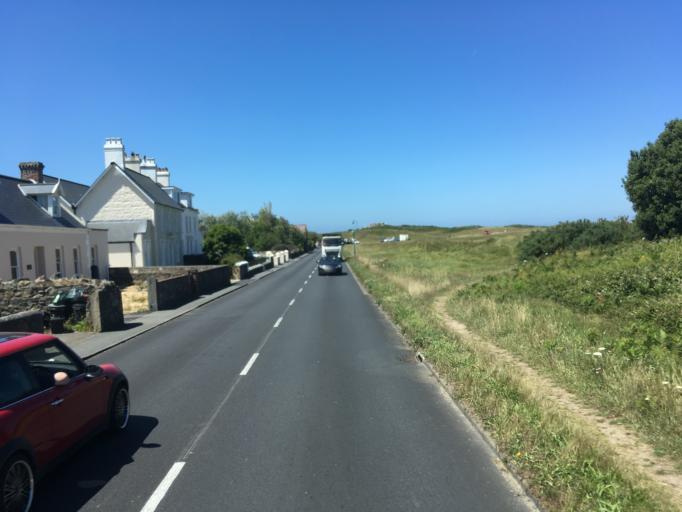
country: GG
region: St Peter Port
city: Saint Peter Port
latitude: 49.4993
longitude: -2.5220
